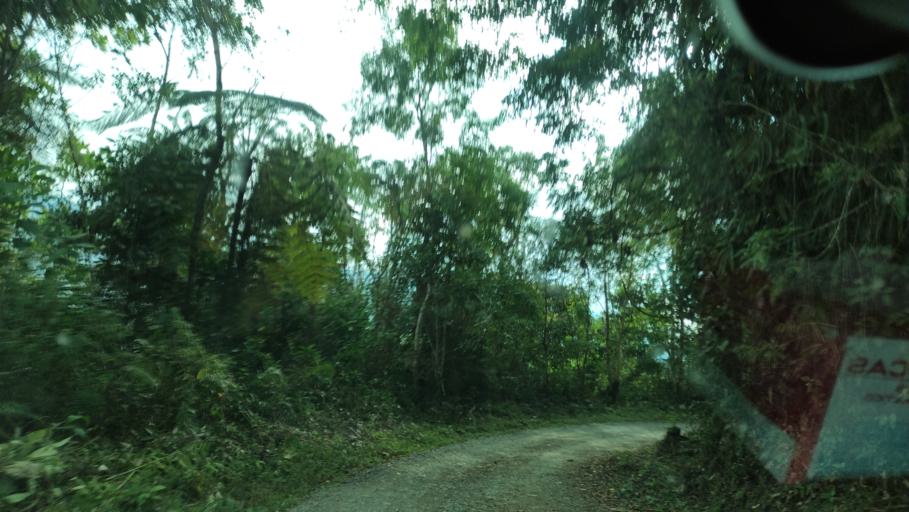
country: CO
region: Valle del Cauca
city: San Pedro
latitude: 3.8812
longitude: -76.1565
